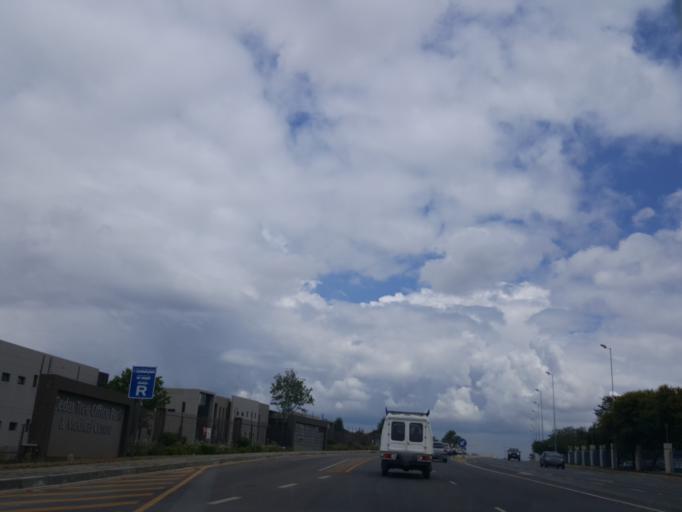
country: ZA
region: Gauteng
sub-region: City of Johannesburg Metropolitan Municipality
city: Diepsloot
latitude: -26.0108
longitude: 27.9947
